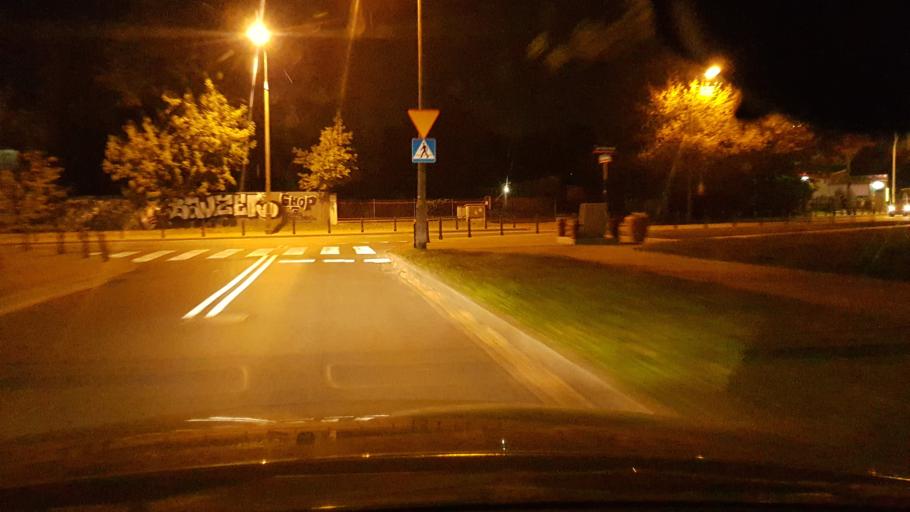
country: PL
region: Masovian Voivodeship
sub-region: Warszawa
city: Praga Polnoc
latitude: 52.2696
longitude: 21.0415
